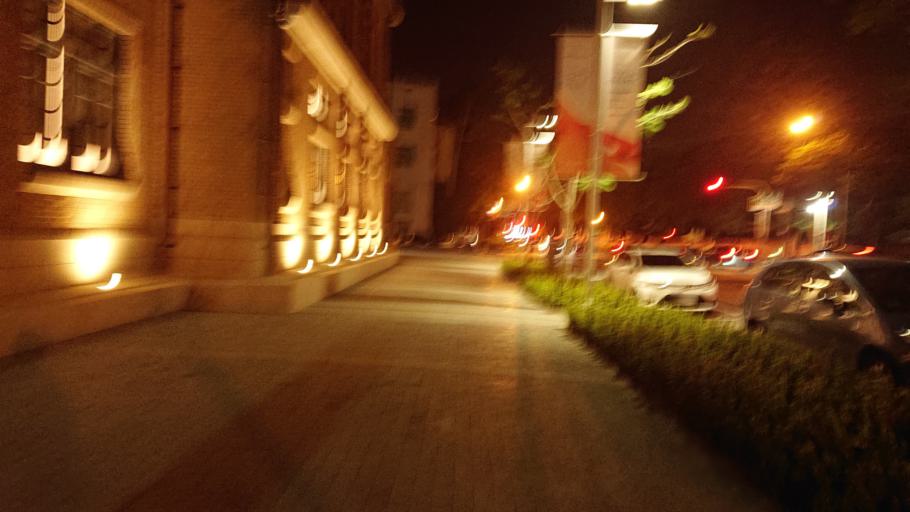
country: TW
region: Taiwan
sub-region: Tainan
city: Tainan
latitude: 22.9913
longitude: 120.2050
